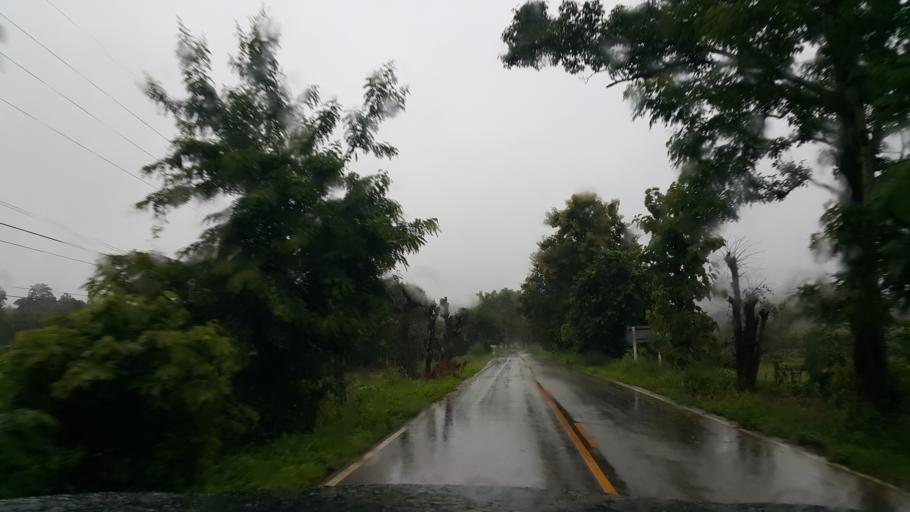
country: TH
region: Phayao
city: Phu Sang
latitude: 19.5937
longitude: 100.3881
